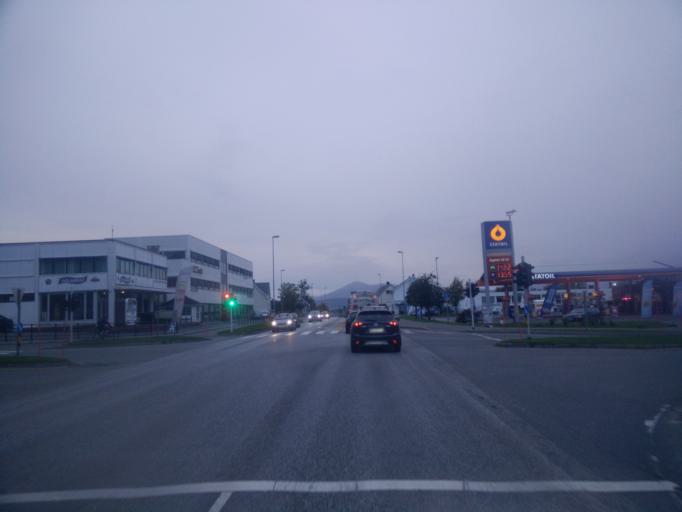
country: NO
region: More og Romsdal
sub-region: Molde
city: Molde
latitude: 62.7397
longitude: 7.1976
